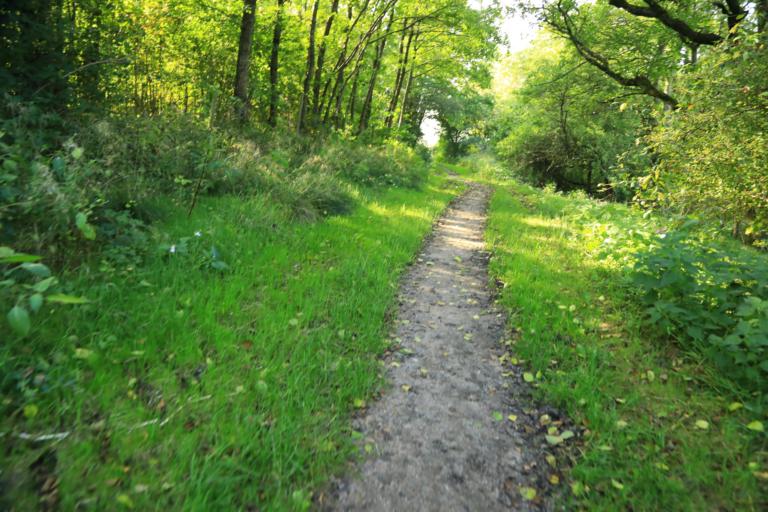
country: SE
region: Halland
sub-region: Varbergs Kommun
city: Varberg
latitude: 57.1297
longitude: 12.2821
